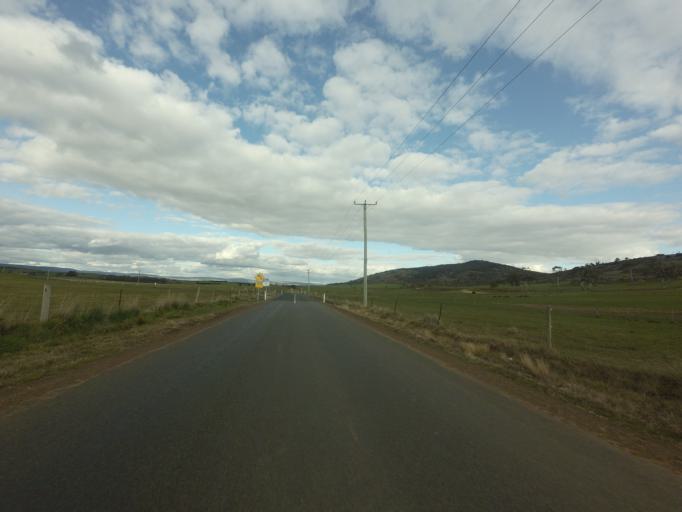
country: AU
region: Tasmania
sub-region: Northern Midlands
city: Evandale
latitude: -41.9120
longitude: 147.3757
